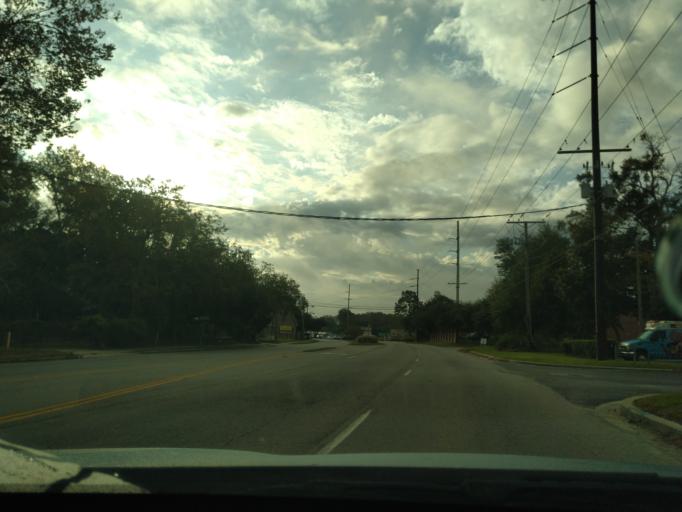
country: US
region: South Carolina
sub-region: Charleston County
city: North Charleston
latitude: 32.7980
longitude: -79.9958
